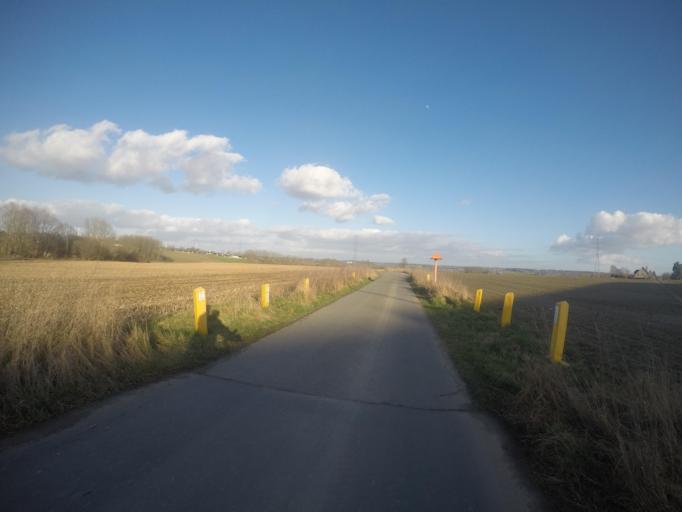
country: BE
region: Wallonia
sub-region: Province du Brabant Wallon
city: Tubize
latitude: 50.7097
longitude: 4.1857
